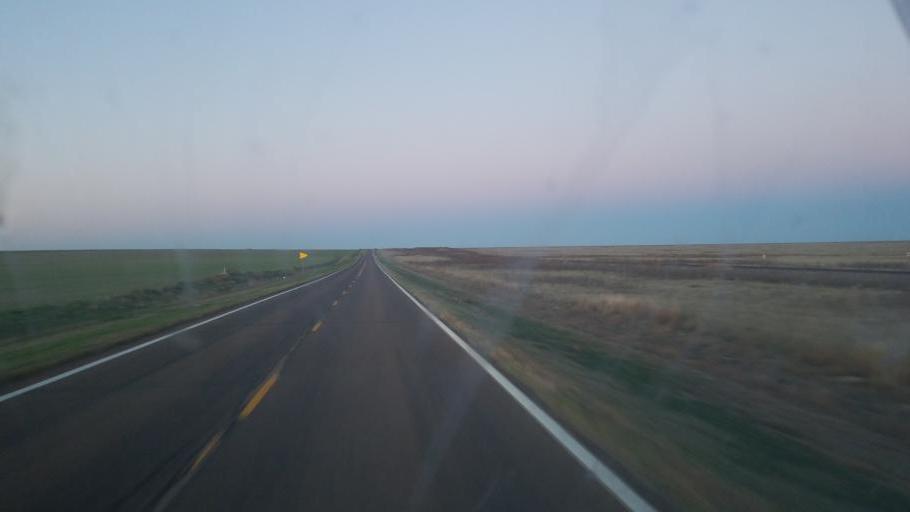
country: US
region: Kansas
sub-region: Wallace County
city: Sharon Springs
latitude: 38.9529
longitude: -101.4812
